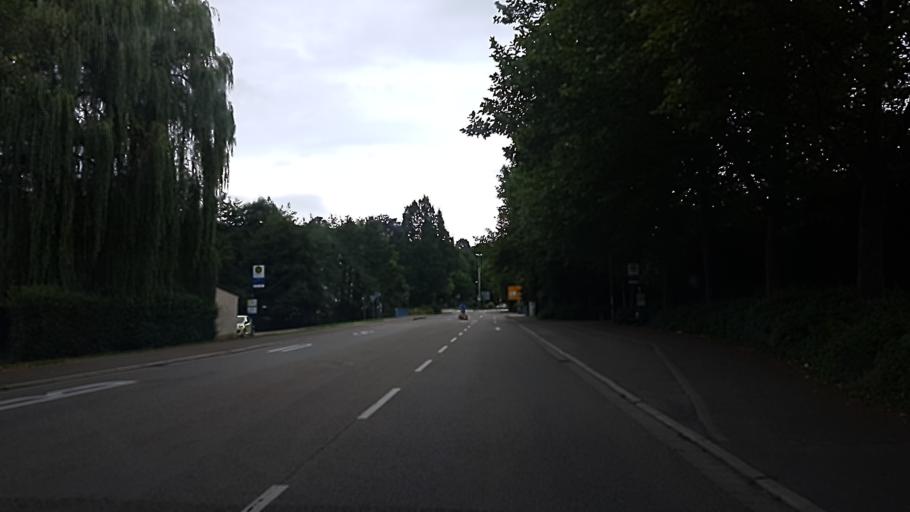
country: DE
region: Baden-Wuerttemberg
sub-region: Freiburg Region
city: Emmendingen
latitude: 48.1170
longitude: 7.8591
